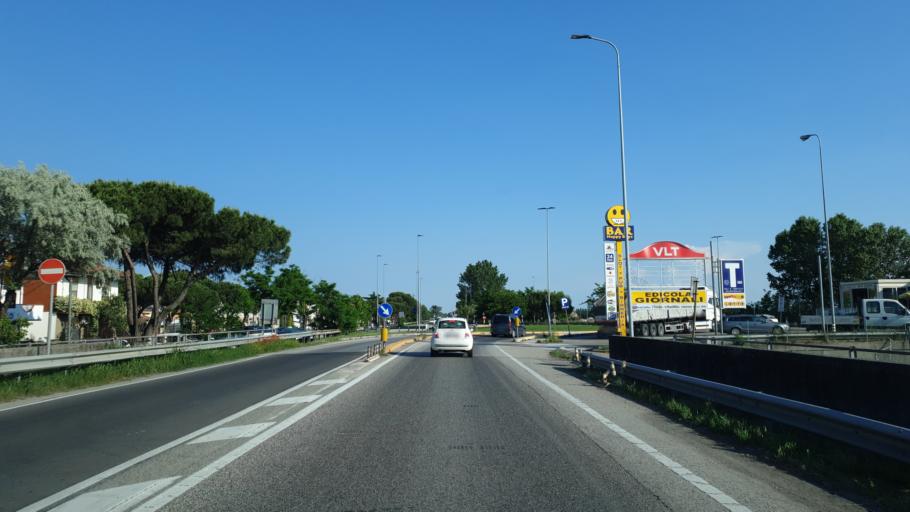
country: IT
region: Emilia-Romagna
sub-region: Provincia di Ravenna
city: Fosso Ghiaia
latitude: 44.3523
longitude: 12.2577
